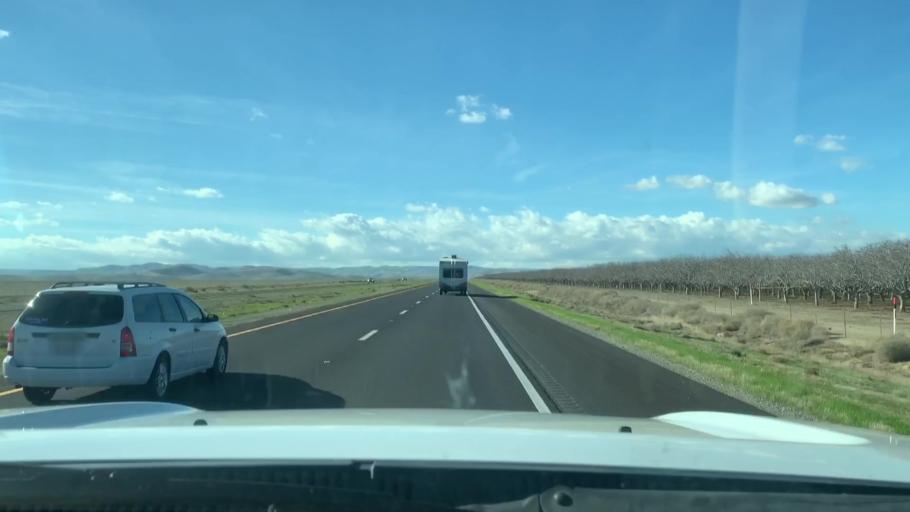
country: US
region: California
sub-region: Kern County
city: Lost Hills
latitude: 35.6147
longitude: -119.9304
